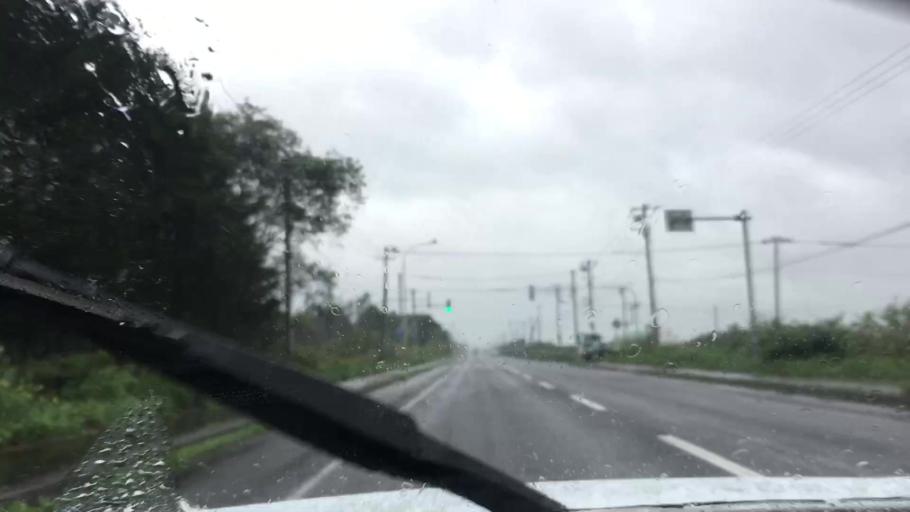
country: JP
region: Hokkaido
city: Nanae
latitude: 42.3132
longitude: 140.2735
